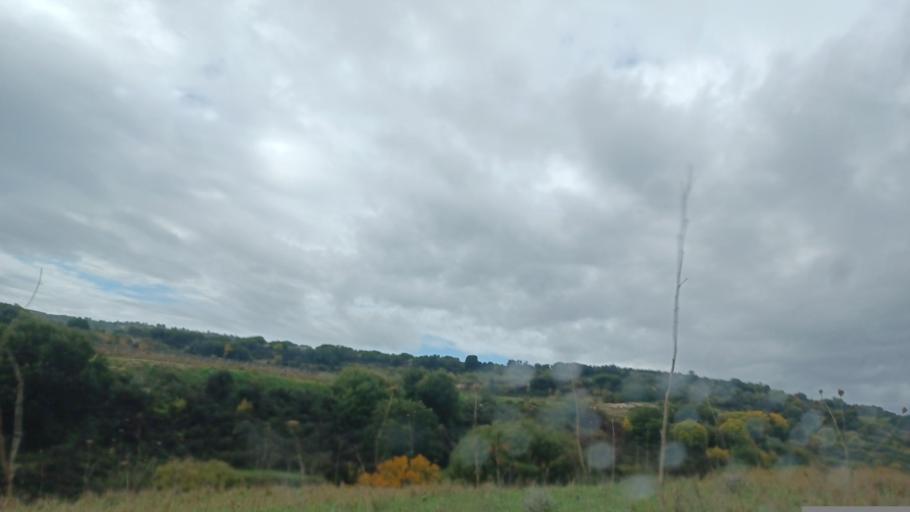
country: CY
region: Pafos
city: Mesogi
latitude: 34.8668
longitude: 32.5347
